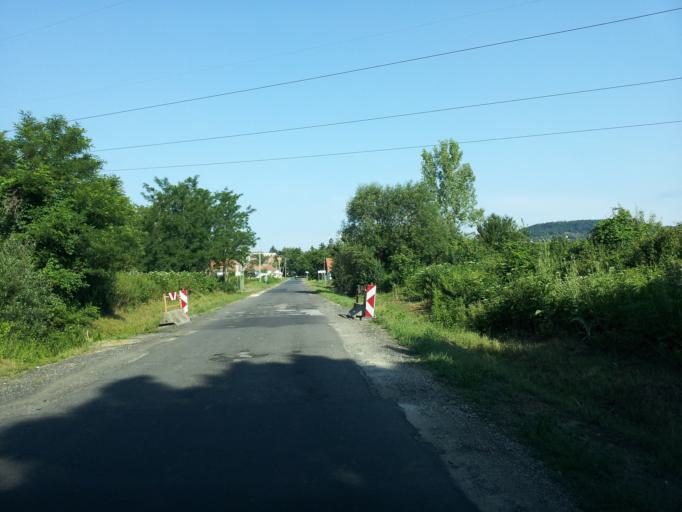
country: HU
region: Zala
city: Cserszegtomaj
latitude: 46.8820
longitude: 17.2331
